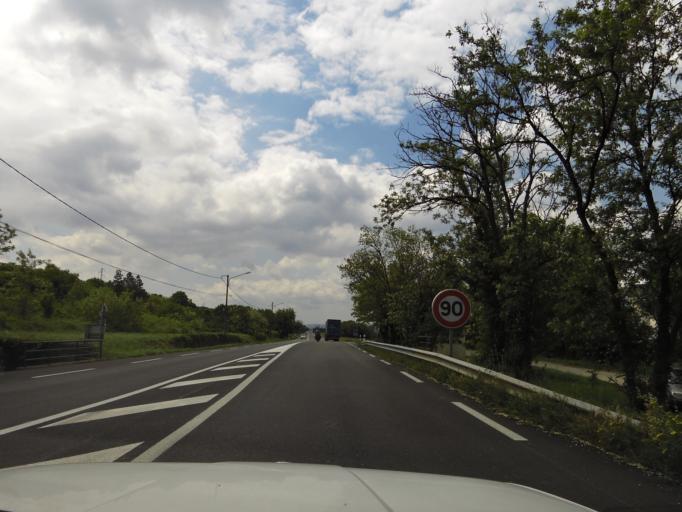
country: FR
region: Rhone-Alpes
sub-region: Departement de l'Ardeche
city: Cruas
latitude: 44.6372
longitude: 4.7731
